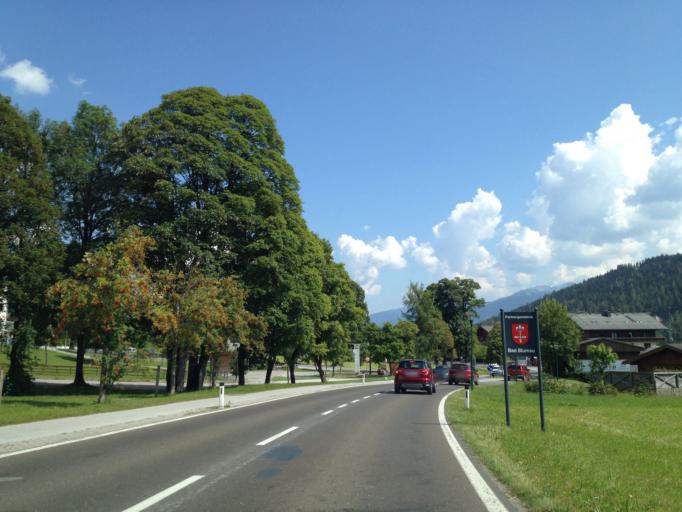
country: AT
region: Styria
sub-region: Politischer Bezirk Liezen
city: Schladming
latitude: 47.4220
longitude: 13.6507
